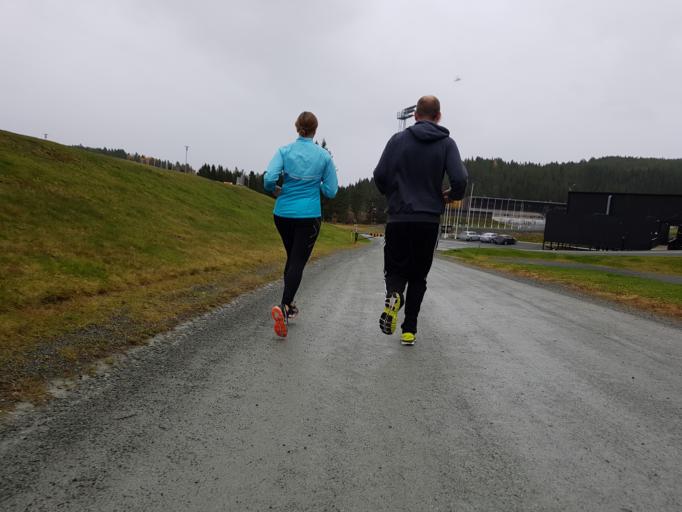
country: NO
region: Sor-Trondelag
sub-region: Melhus
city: Melhus
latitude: 63.3785
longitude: 10.3076
